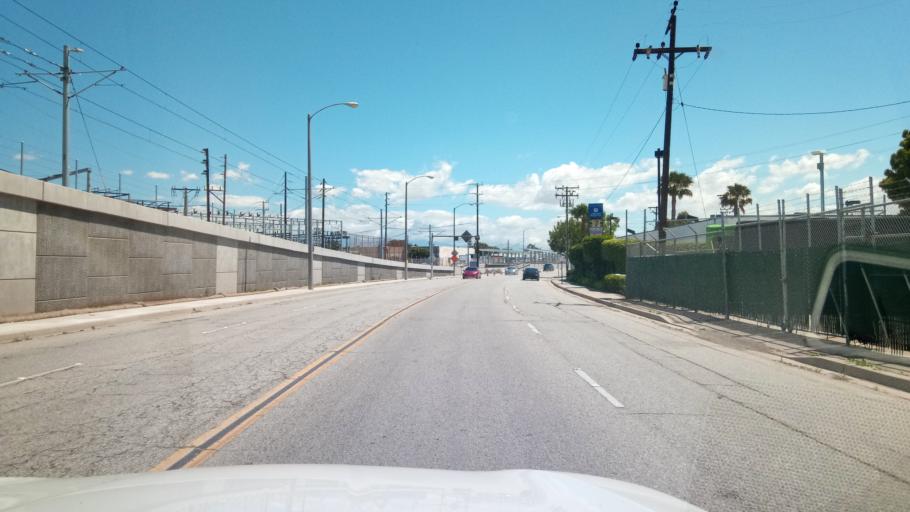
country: US
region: California
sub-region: Los Angeles County
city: Inglewood
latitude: 33.9608
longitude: -118.3765
